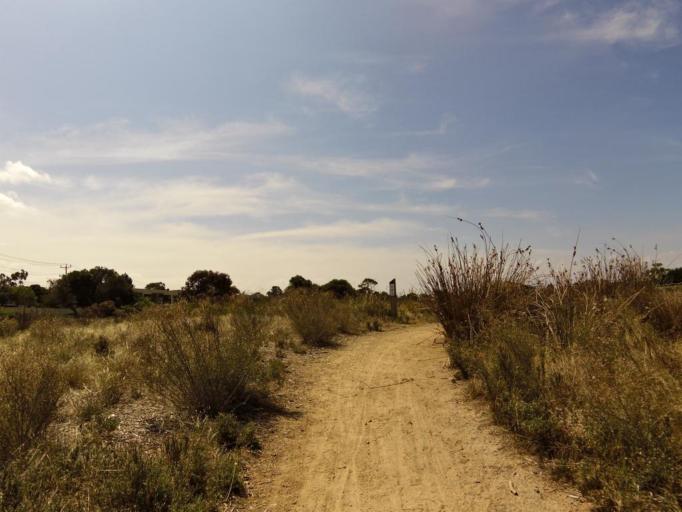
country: AU
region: Victoria
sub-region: Mornington Peninsula
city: Hastings
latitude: -38.3150
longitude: 145.1942
